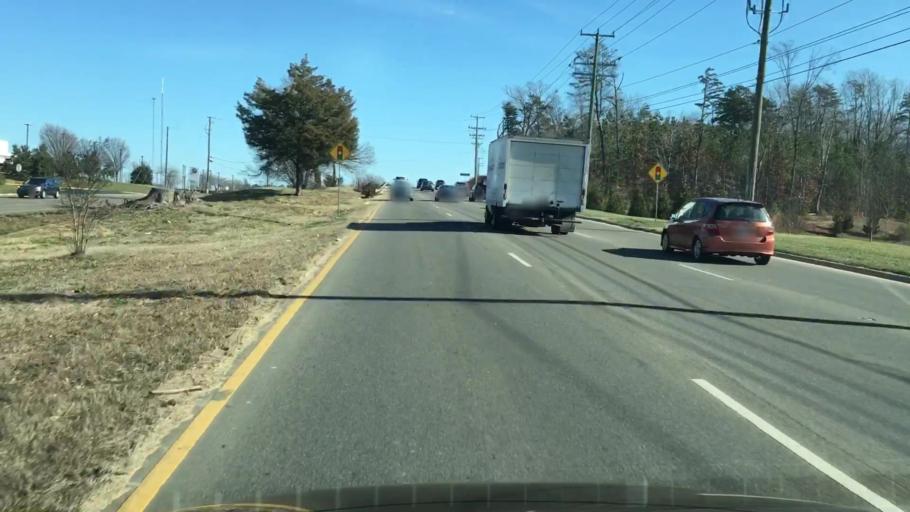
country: US
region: Virginia
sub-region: Chesterfield County
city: Bon Air
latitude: 37.5038
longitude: -77.6245
